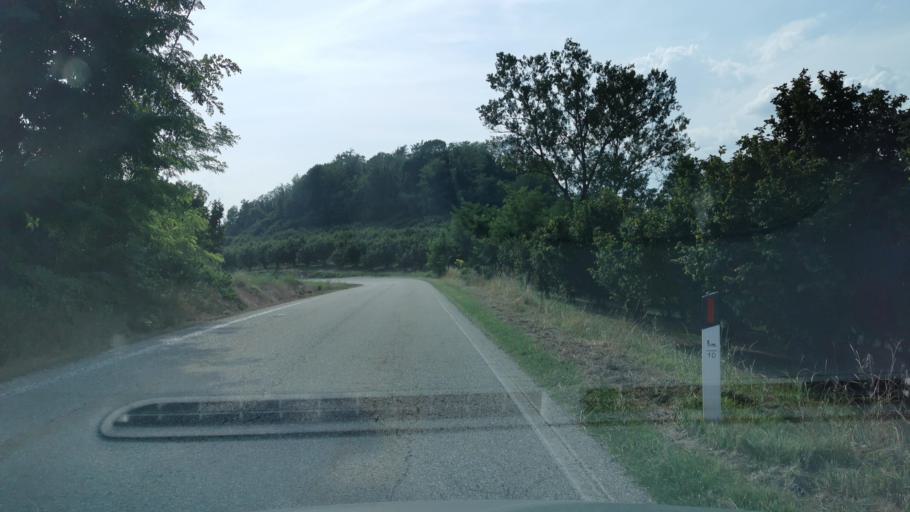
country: IT
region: Piedmont
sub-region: Provincia di Cuneo
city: Cherasco
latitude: 44.6481
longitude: 7.8886
